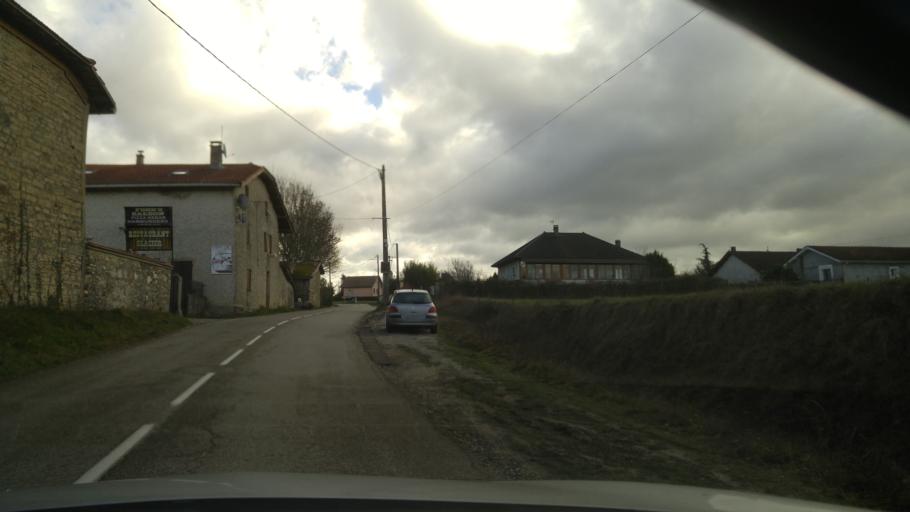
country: FR
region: Rhone-Alpes
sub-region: Departement de l'Isere
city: Roche
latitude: 45.5832
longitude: 5.1684
